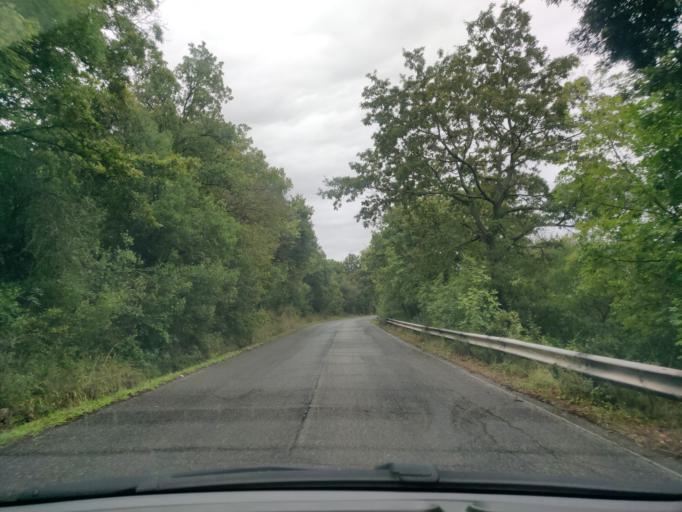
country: IT
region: Latium
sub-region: Citta metropolitana di Roma Capitale
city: Allumiere
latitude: 42.1285
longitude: 11.8560
